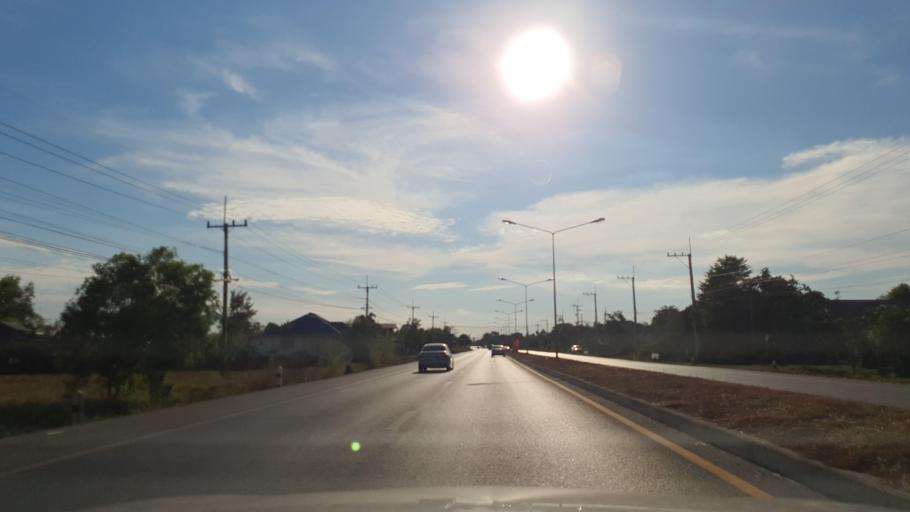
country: TH
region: Maha Sarakham
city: Kantharawichai
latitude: 16.3518
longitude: 103.3276
